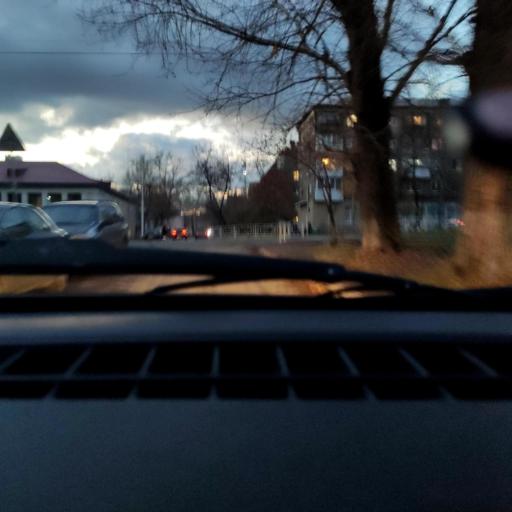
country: RU
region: Bashkortostan
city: Ufa
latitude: 54.8119
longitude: 56.0824
